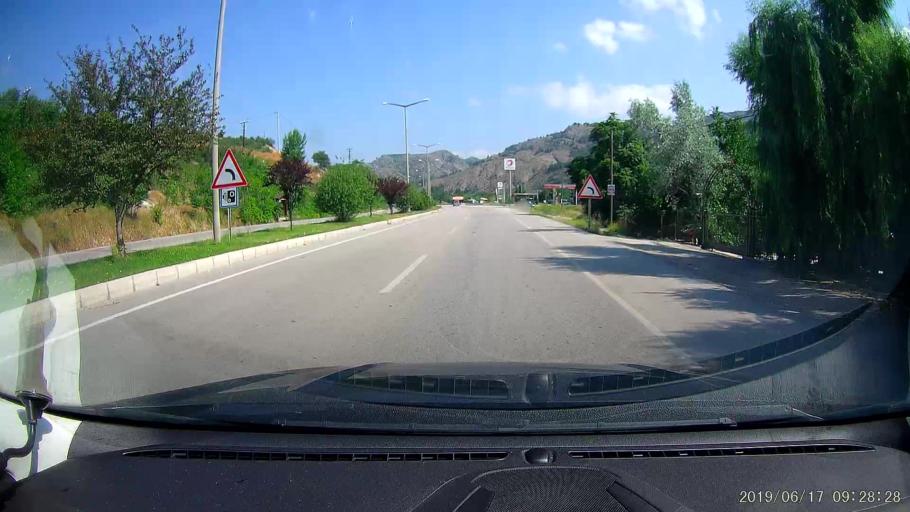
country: TR
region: Amasya
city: Amasya
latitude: 40.6886
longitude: 35.8222
